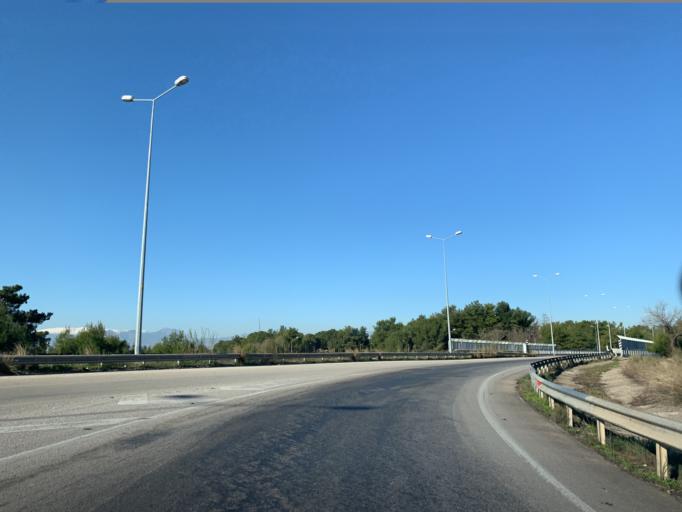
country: TR
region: Antalya
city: Aksu
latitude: 36.9446
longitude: 30.8322
